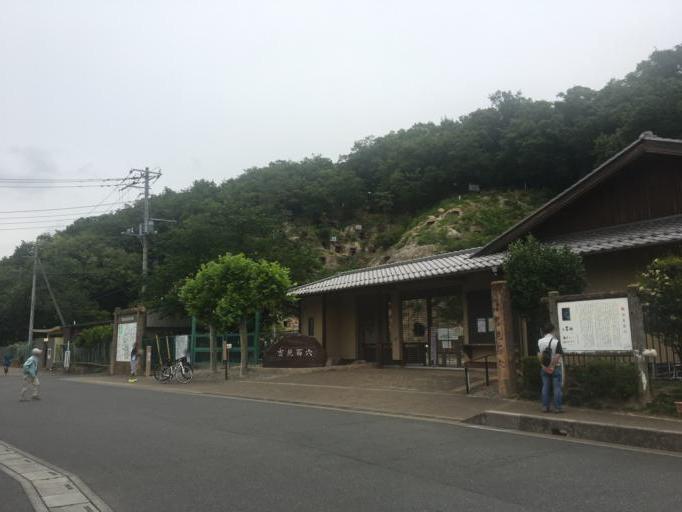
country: JP
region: Saitama
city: Fukiage-fujimi
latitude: 36.0391
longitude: 139.4210
